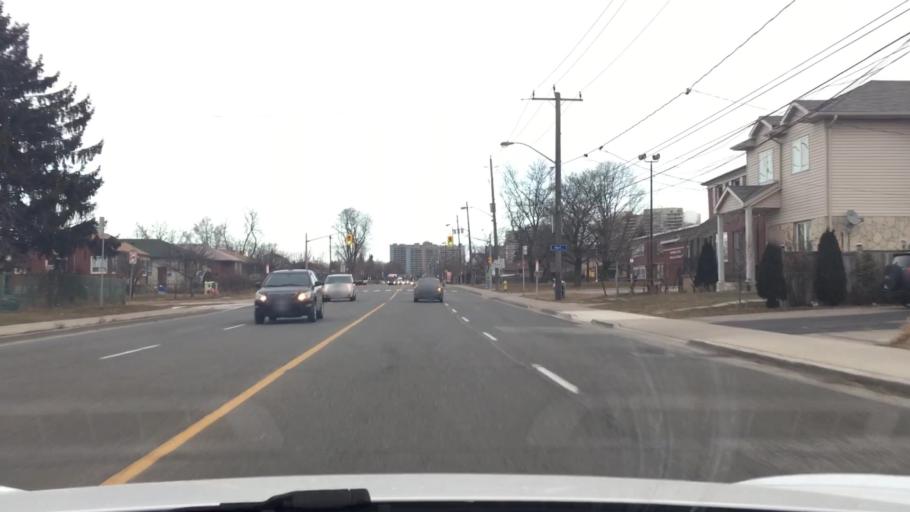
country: CA
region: Ontario
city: Scarborough
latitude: 43.7184
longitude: -79.2590
